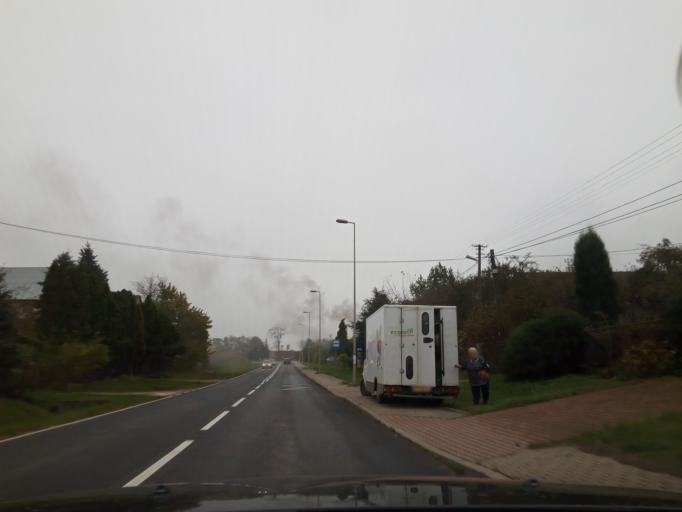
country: PL
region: Lesser Poland Voivodeship
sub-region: Powiat proszowicki
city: Klimontow
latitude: 50.2269
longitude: 20.3437
